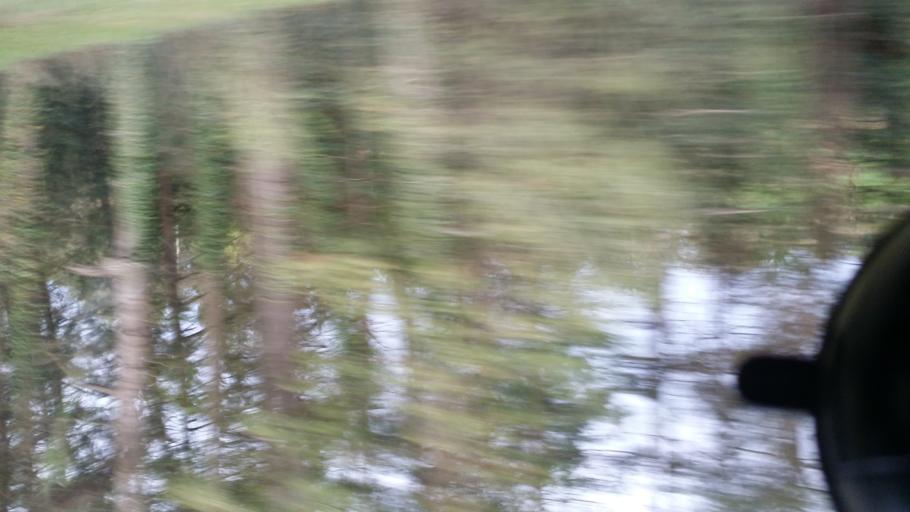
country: IE
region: Ulster
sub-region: An Cabhan
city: Virginia
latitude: 53.8477
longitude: -7.0991
